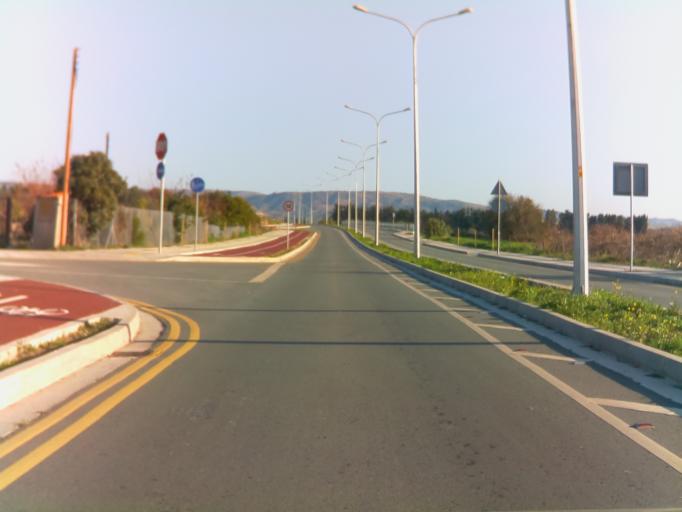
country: CY
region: Pafos
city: Paphos
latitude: 34.7356
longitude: 32.4620
